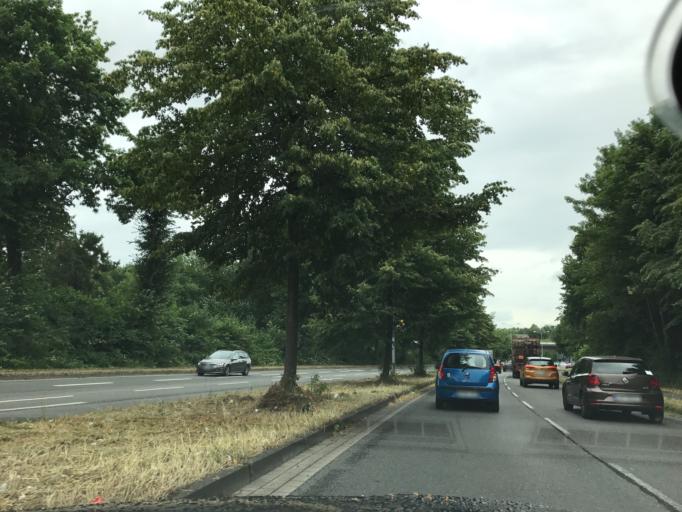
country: DE
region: North Rhine-Westphalia
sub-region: Regierungsbezirk Dusseldorf
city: Muelheim (Ruhr)
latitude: 51.4318
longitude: 6.9294
